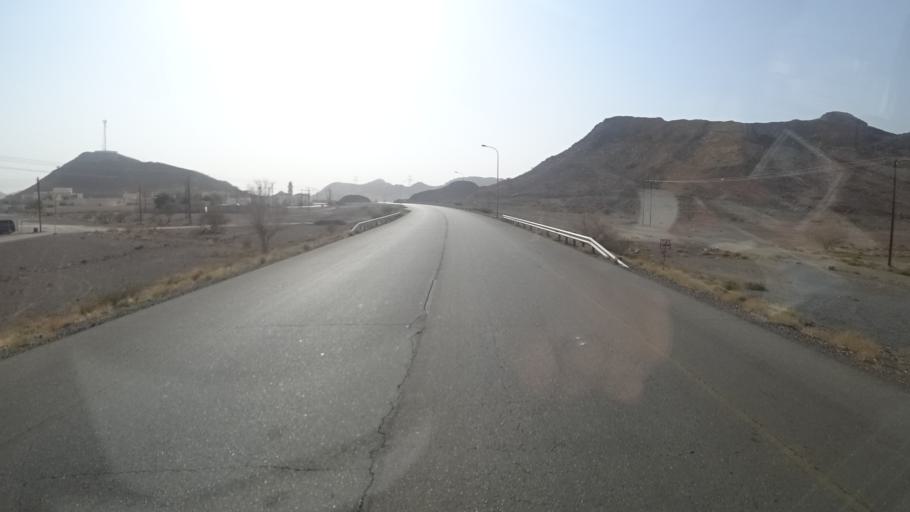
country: OM
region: Muhafazat ad Dakhiliyah
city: Izki
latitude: 22.7924
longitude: 57.8067
